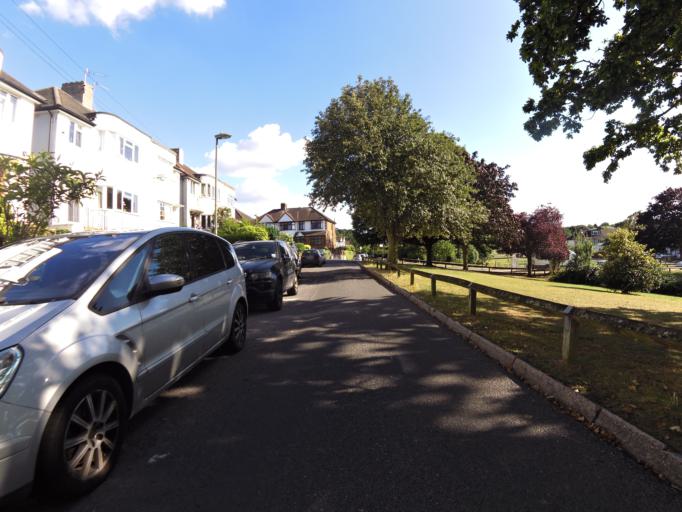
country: GB
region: England
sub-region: Greater London
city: Hadley Wood
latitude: 51.6327
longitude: -0.1464
